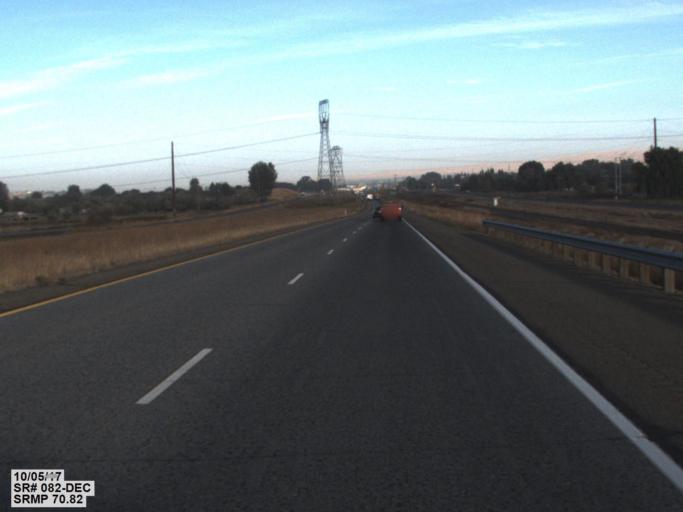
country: US
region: Washington
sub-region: Yakima County
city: Grandview
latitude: 46.2894
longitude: -119.9492
